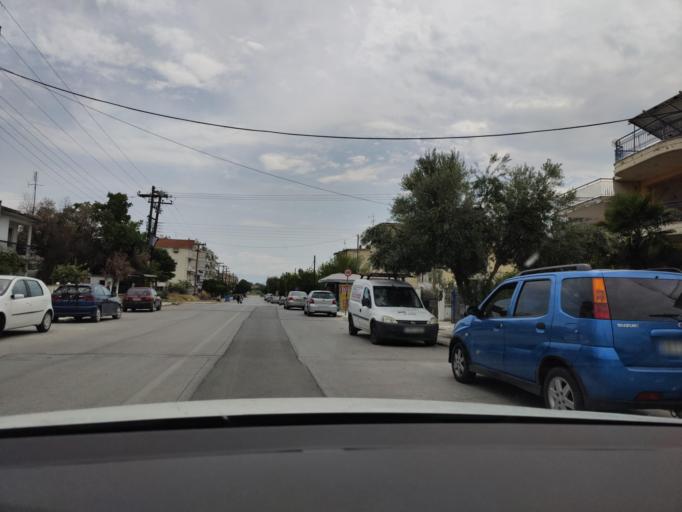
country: GR
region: Central Macedonia
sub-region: Nomos Serron
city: Serres
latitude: 41.0816
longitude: 23.5371
